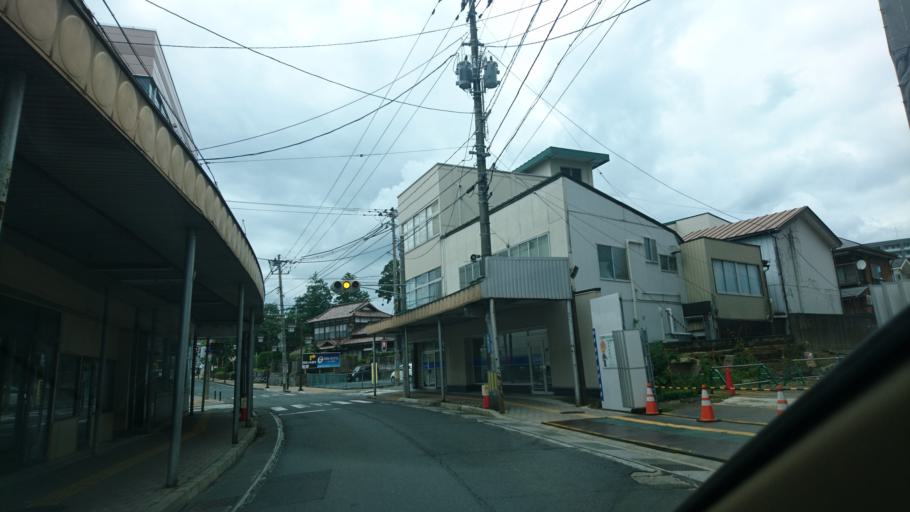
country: JP
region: Iwate
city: Kitakami
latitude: 39.2852
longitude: 141.1199
